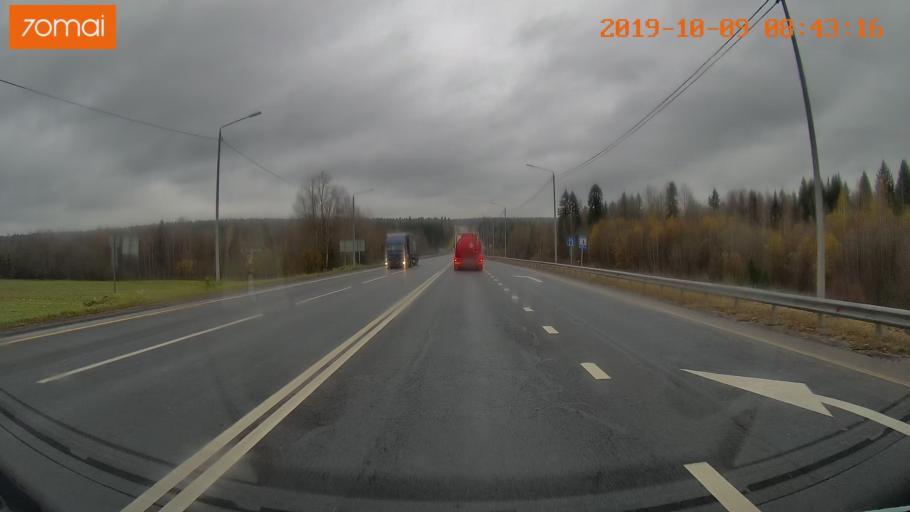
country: RU
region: Vologda
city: Gryazovets
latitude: 59.0226
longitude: 40.1151
